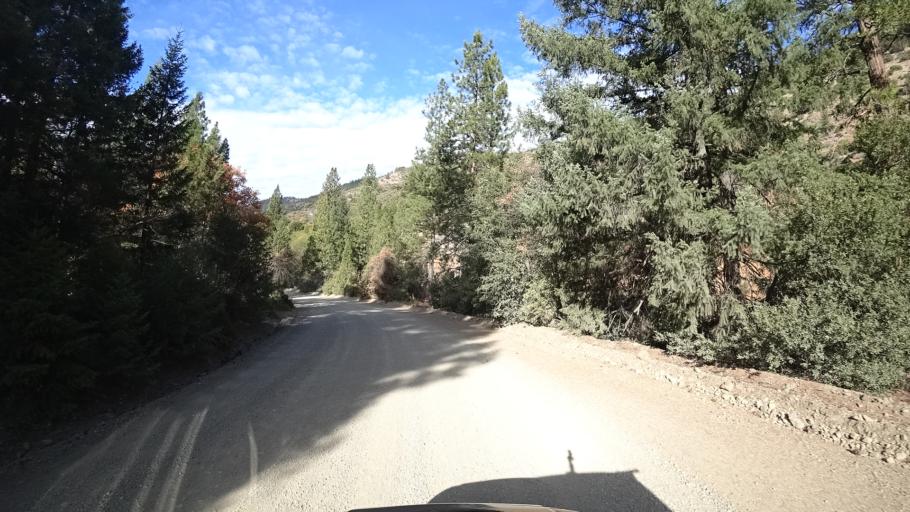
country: US
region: California
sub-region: Siskiyou County
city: Yreka
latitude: 41.7162
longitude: -122.7917
